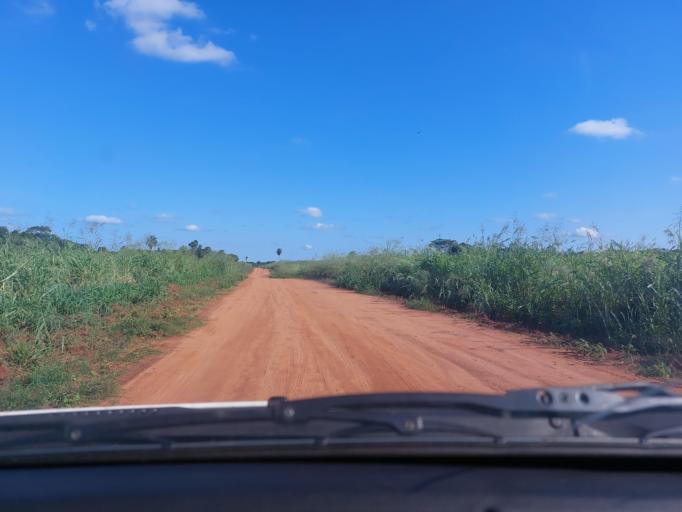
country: PY
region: San Pedro
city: Guayaybi
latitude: -24.5176
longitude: -56.5463
